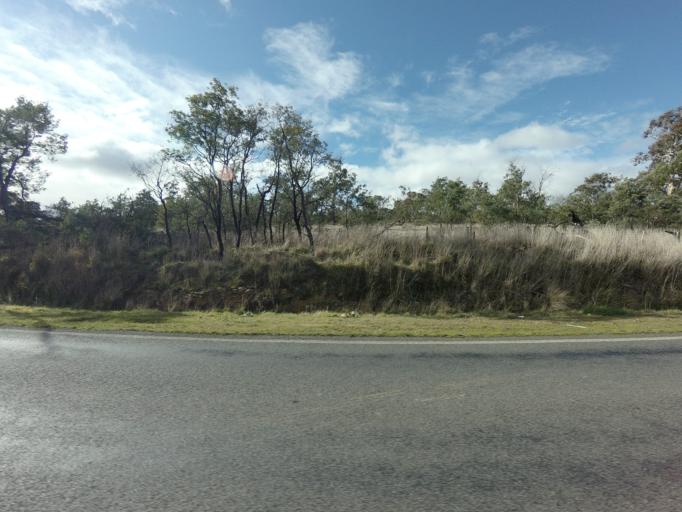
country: AU
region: Tasmania
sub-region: Derwent Valley
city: New Norfolk
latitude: -42.6008
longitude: 146.8864
